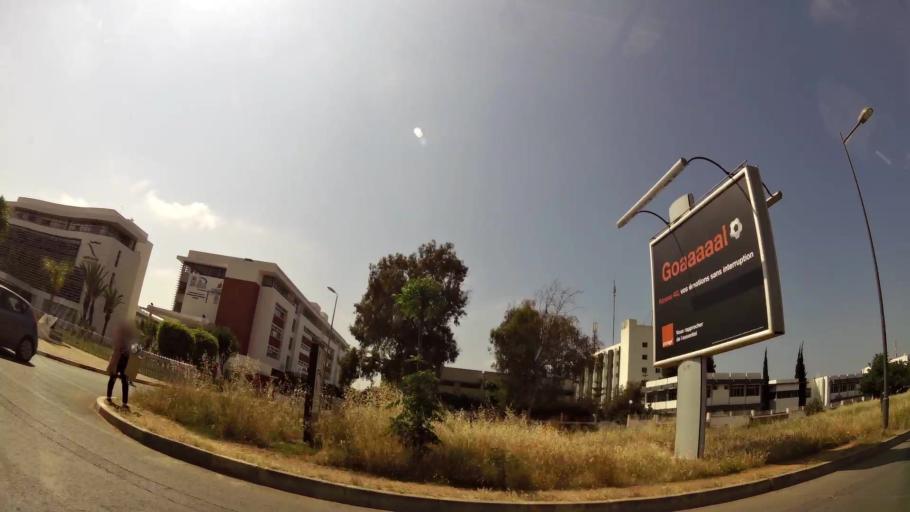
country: MA
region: Rabat-Sale-Zemmour-Zaer
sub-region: Rabat
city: Rabat
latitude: 33.9786
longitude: -6.8670
